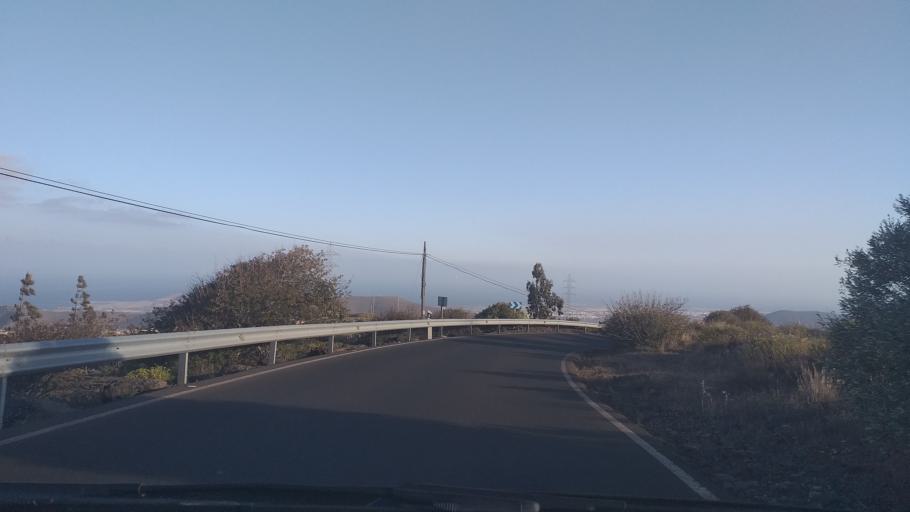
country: ES
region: Canary Islands
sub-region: Provincia de Las Palmas
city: Ingenio
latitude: 27.9294
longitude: -15.4564
